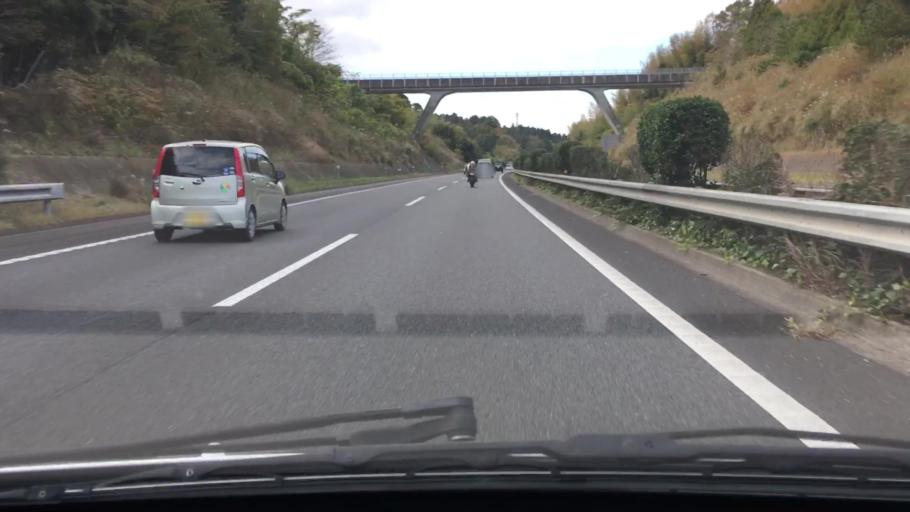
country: JP
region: Chiba
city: Ichihara
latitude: 35.4459
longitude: 140.0731
